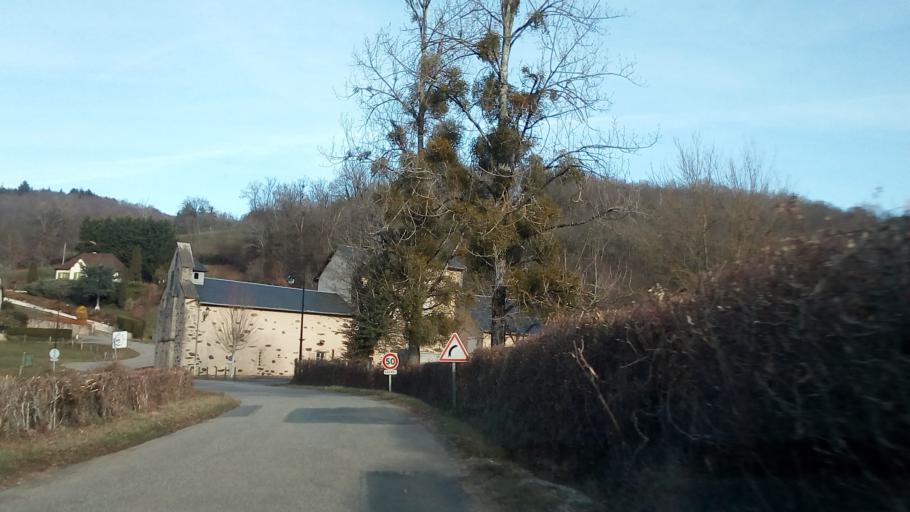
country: FR
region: Limousin
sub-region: Departement de la Correze
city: Naves
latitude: 45.3064
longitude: 1.7965
